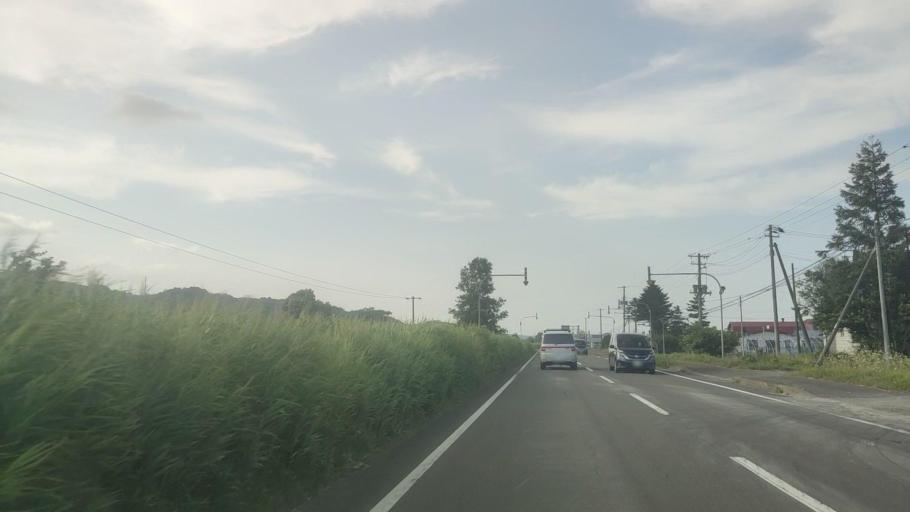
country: JP
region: Hokkaido
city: Iwamizawa
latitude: 42.9892
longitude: 141.7914
